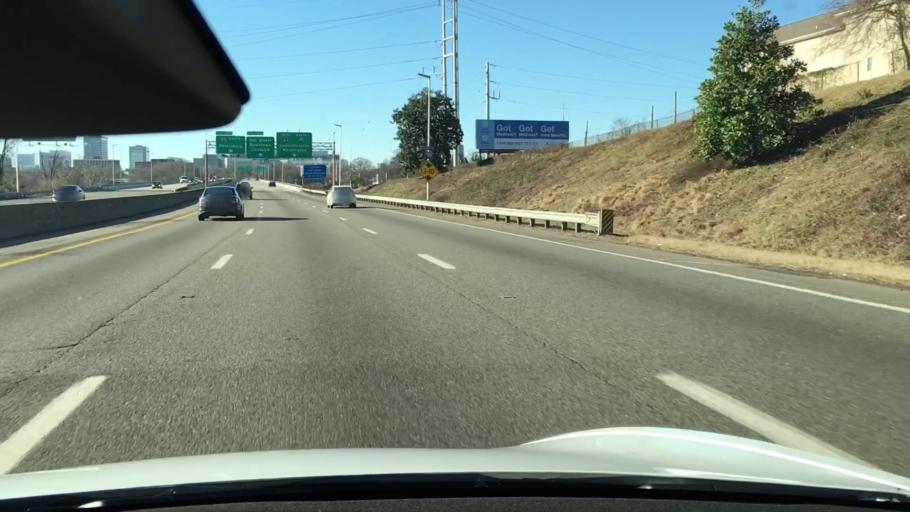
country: US
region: Virginia
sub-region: Henrico County
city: East Highland Park
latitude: 37.5560
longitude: -77.4256
